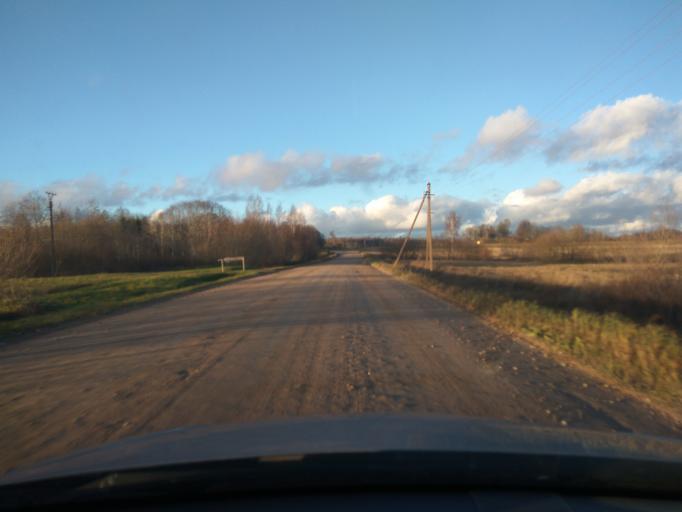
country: LV
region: Aizpute
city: Aizpute
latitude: 56.8156
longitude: 21.7784
